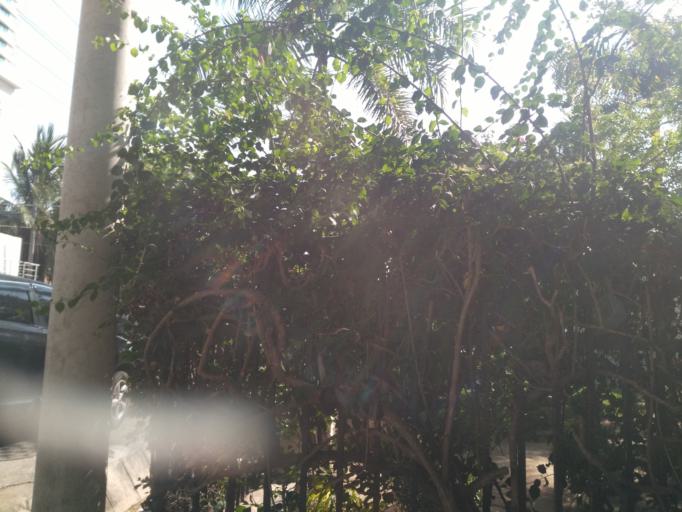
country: TZ
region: Dar es Salaam
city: Dar es Salaam
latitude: -6.8093
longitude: 39.2860
